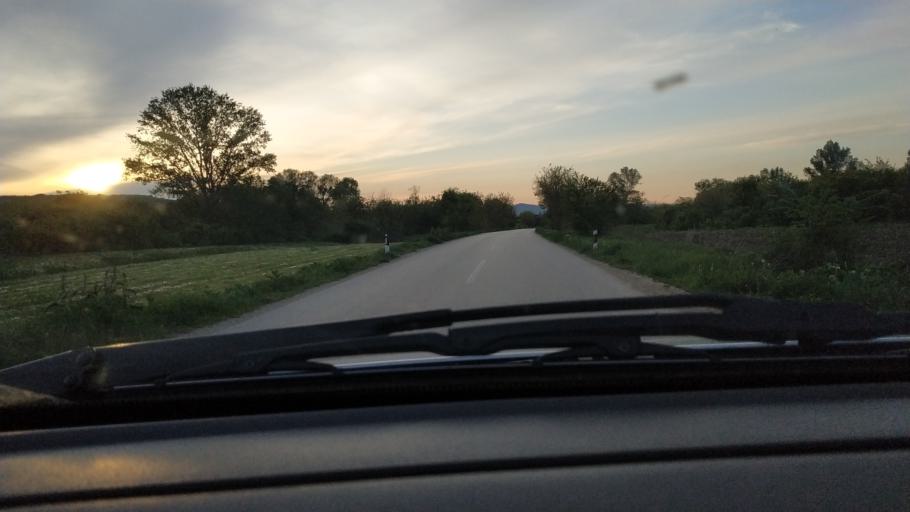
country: RS
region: Central Serbia
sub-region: Nisavski Okrug
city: Aleksinac
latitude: 43.5492
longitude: 21.6201
